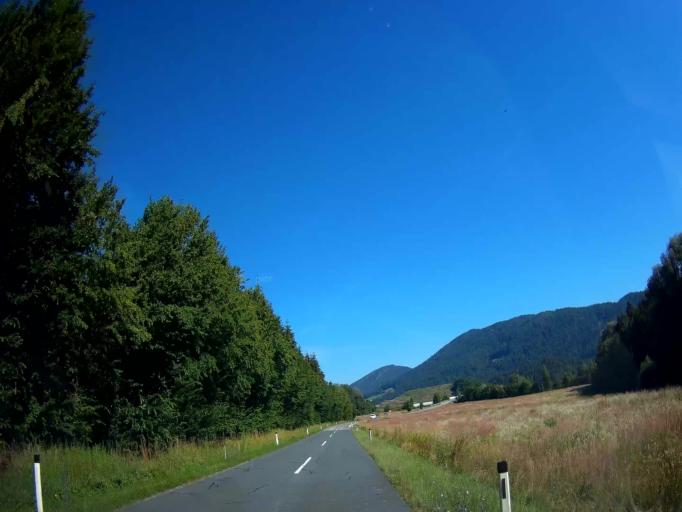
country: AT
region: Carinthia
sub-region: Politischer Bezirk Volkermarkt
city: Voelkermarkt
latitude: 46.6427
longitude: 14.5489
